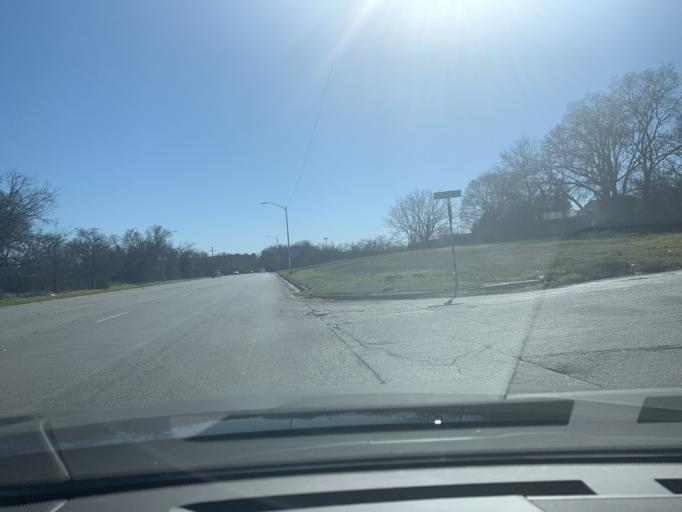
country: US
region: Texas
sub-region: Tarrant County
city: Haltom City
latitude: 32.7624
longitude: -97.2878
